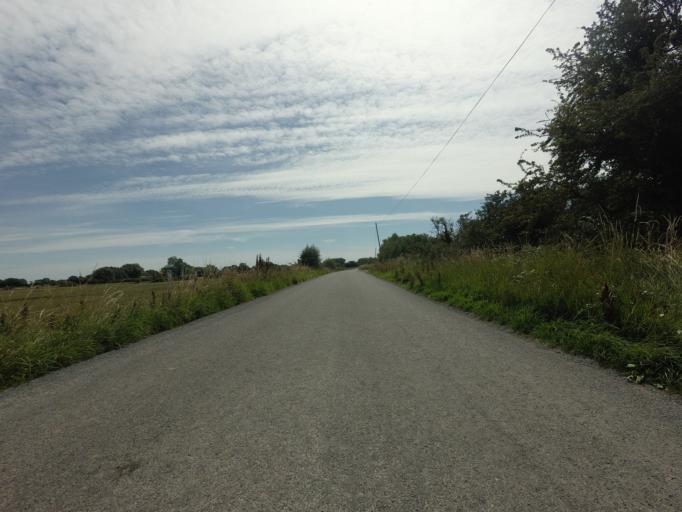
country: GB
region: England
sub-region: Kent
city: Stone
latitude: 51.0028
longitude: 0.8013
